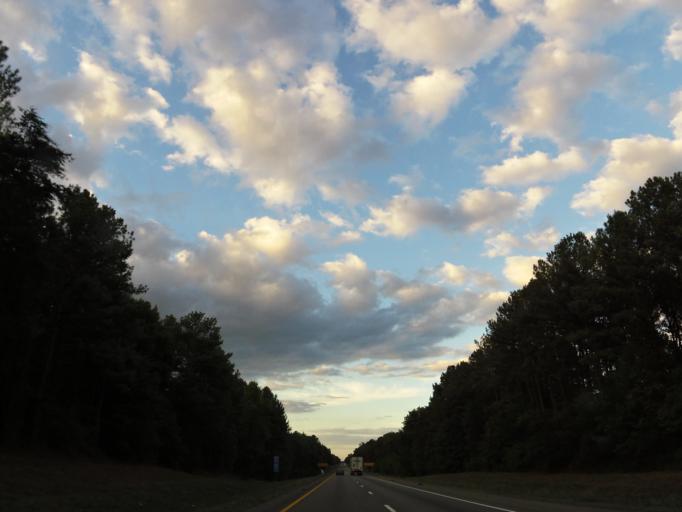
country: US
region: Tennessee
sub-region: Bradley County
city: Hopewell
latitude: 35.2429
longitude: -84.8448
